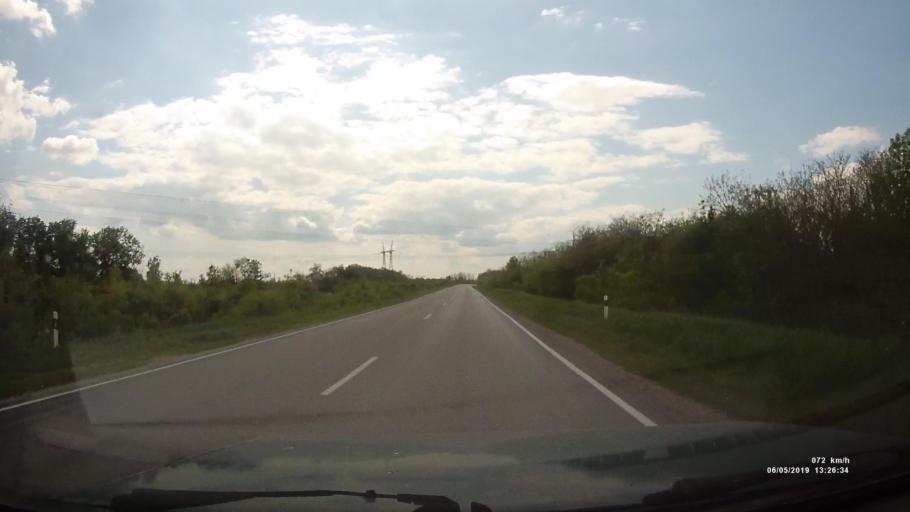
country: RU
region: Rostov
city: Ust'-Donetskiy
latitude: 47.6771
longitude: 40.8948
